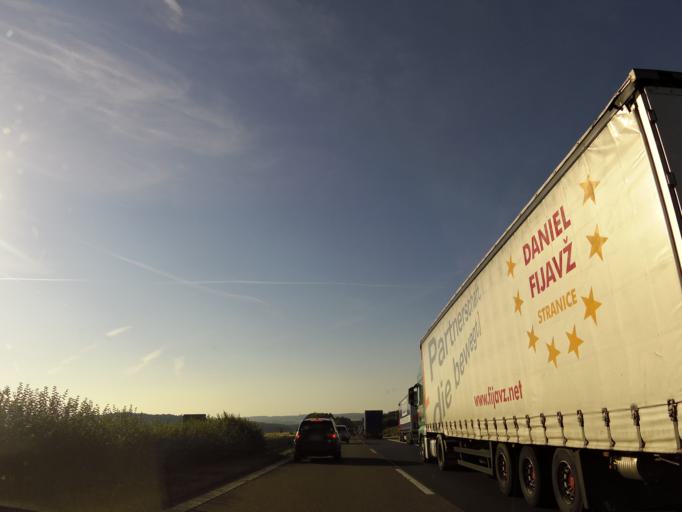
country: DE
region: Bavaria
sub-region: Regierungsbezirk Mittelfranken
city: Gremsdorf
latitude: 49.7189
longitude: 10.8342
